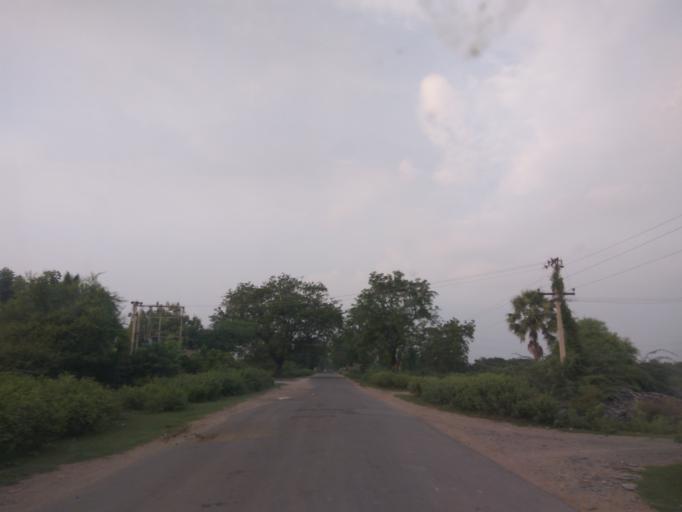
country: IN
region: Andhra Pradesh
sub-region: Guntur
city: Vinukonda
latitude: 16.0844
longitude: 79.7460
